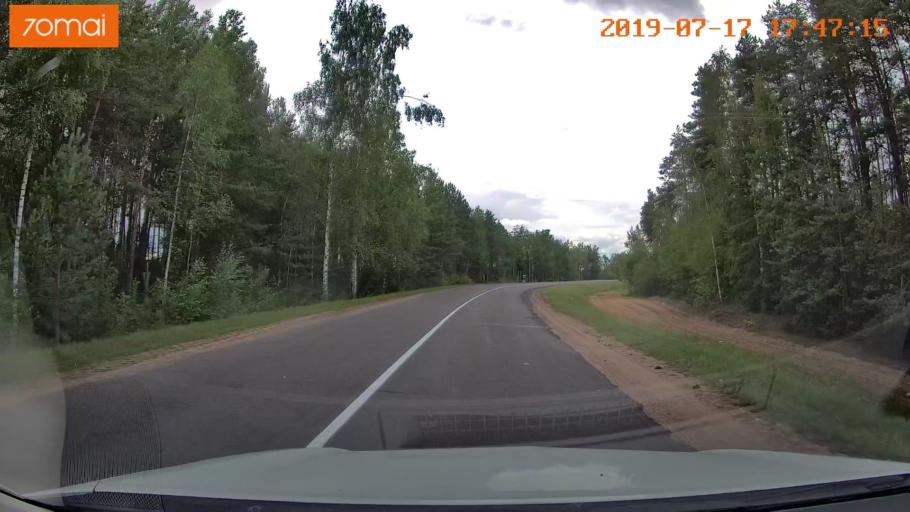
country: BY
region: Mogilev
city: Hlusha
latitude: 53.1080
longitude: 28.8295
